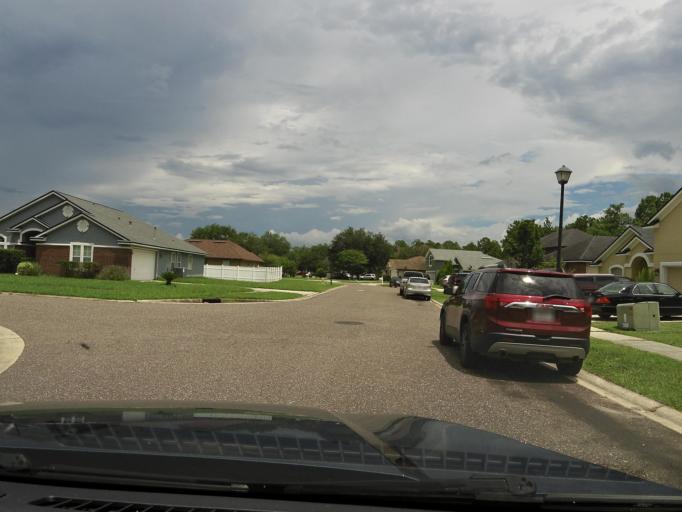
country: US
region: Florida
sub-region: Duval County
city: Jacksonville
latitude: 30.4239
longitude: -81.7285
